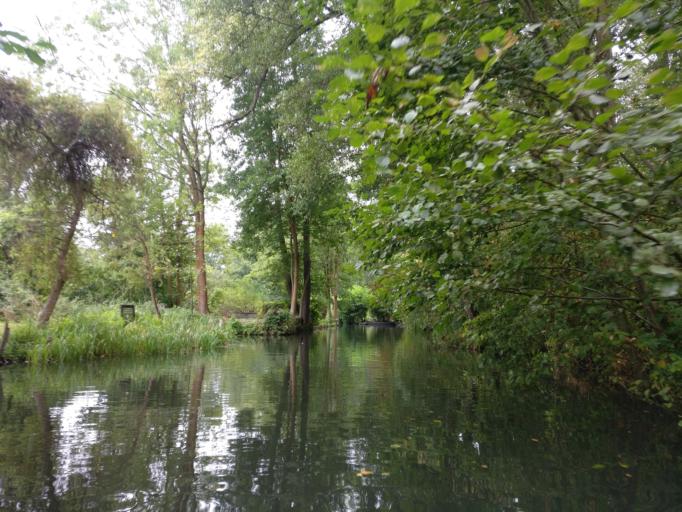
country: DE
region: Brandenburg
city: Lubbenau
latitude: 51.8679
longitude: 13.9950
